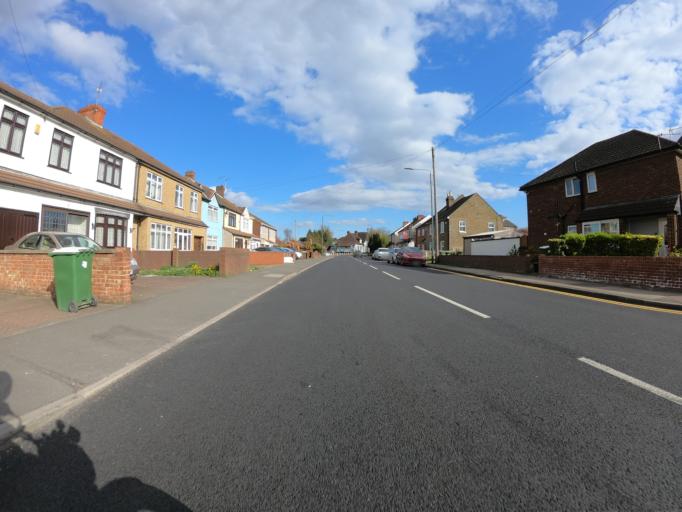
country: GB
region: England
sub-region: Greater London
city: Bexleyheath
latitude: 51.4642
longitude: 0.1497
